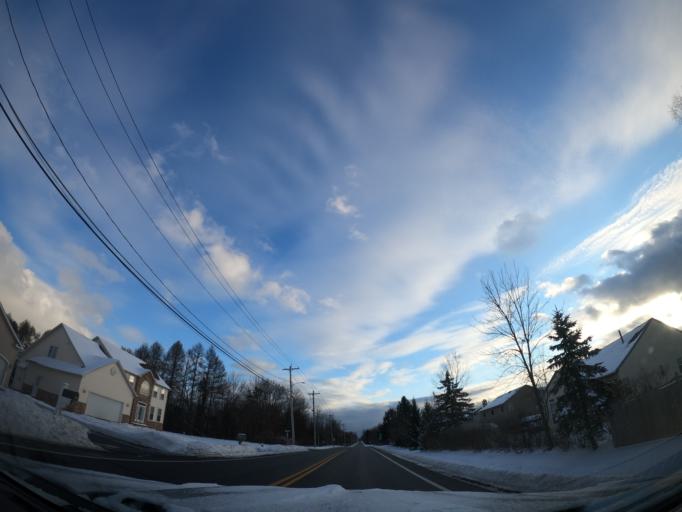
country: US
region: New York
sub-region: Onondaga County
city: Brewerton
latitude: 43.2284
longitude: -76.1127
